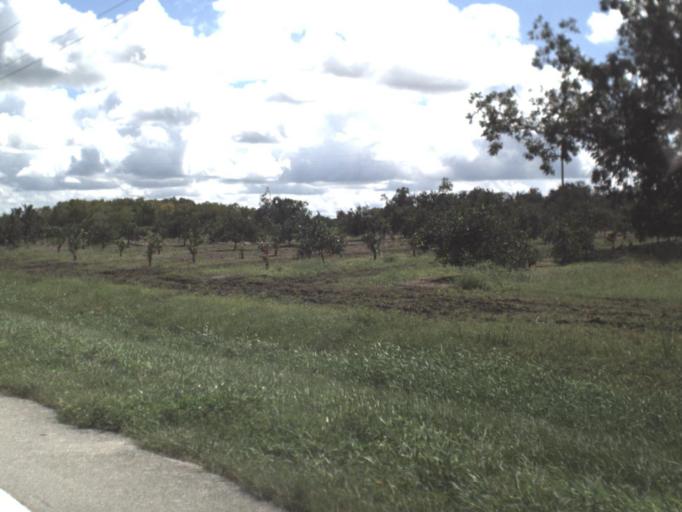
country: US
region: Florida
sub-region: DeSoto County
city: Arcadia
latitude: 27.2530
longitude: -81.9622
